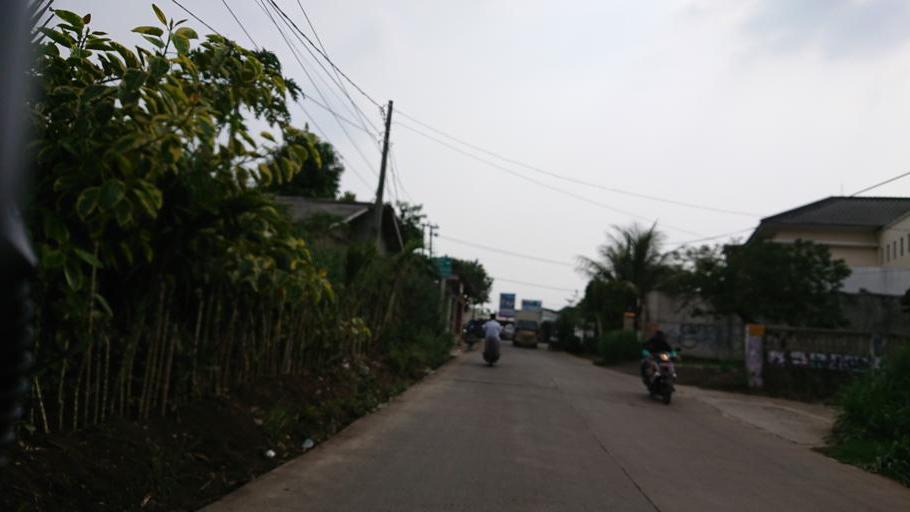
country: ID
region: West Java
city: Parung
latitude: -6.3902
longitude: 106.6831
